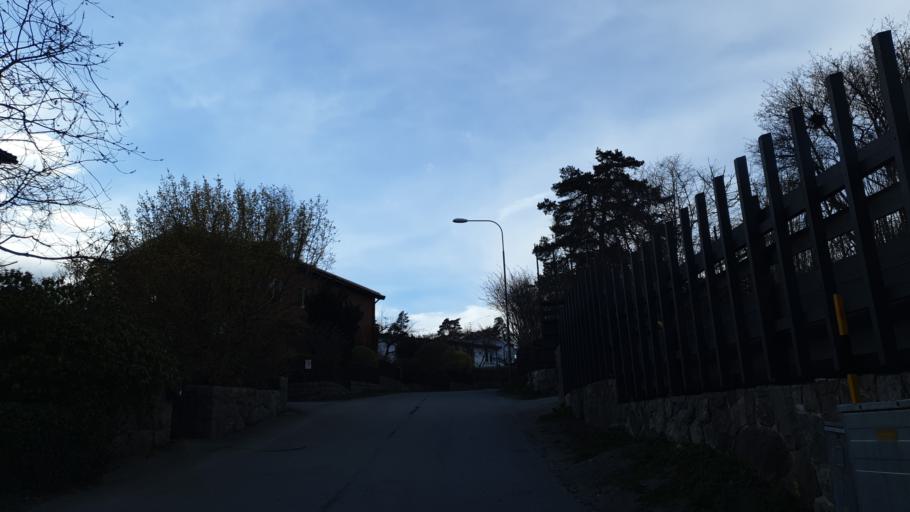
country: SE
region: Stockholm
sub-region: Lidingo
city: Lidingoe
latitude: 59.3709
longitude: 18.1221
